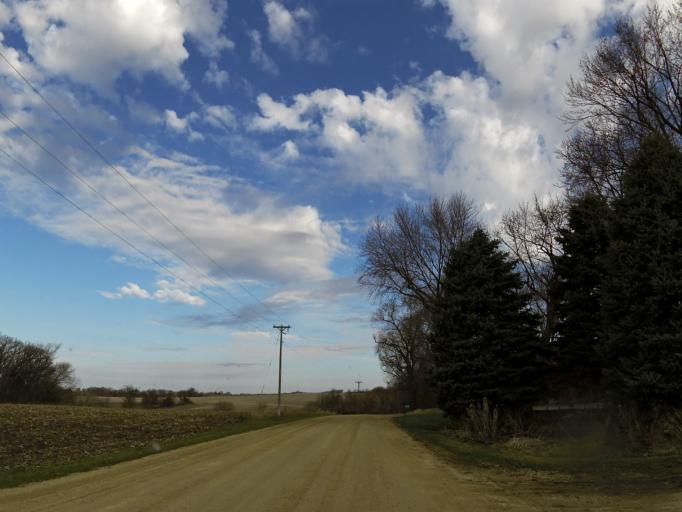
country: US
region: Minnesota
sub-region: Dakota County
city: Hastings
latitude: 44.7633
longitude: -92.8346
